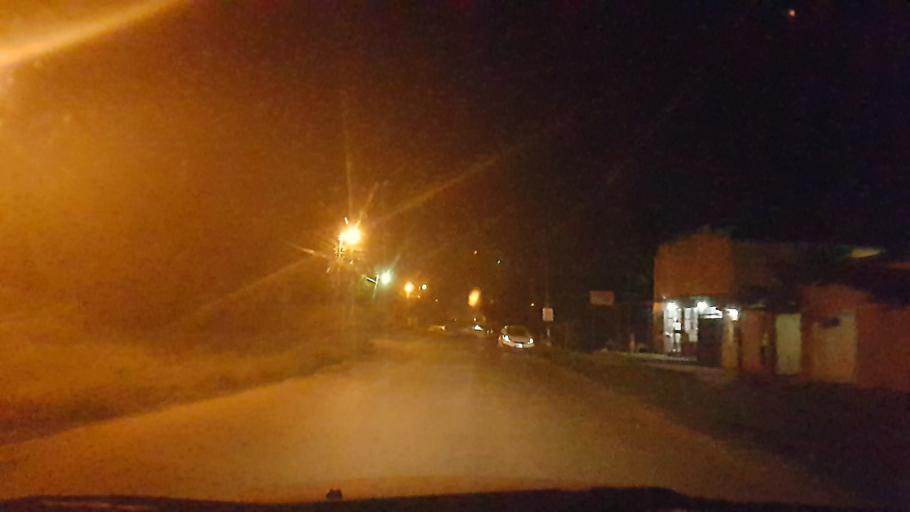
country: PY
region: Central
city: Colonia Mariano Roque Alonso
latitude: -25.1875
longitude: -57.5247
